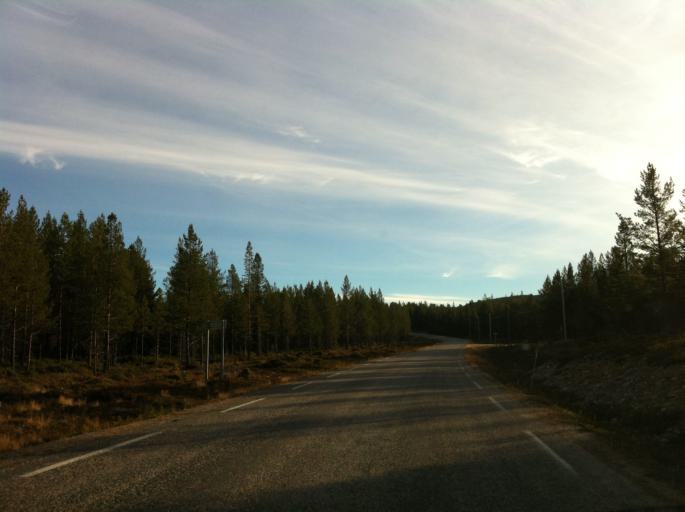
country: NO
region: Hedmark
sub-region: Engerdal
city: Engerdal
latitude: 62.1555
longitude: 11.9486
